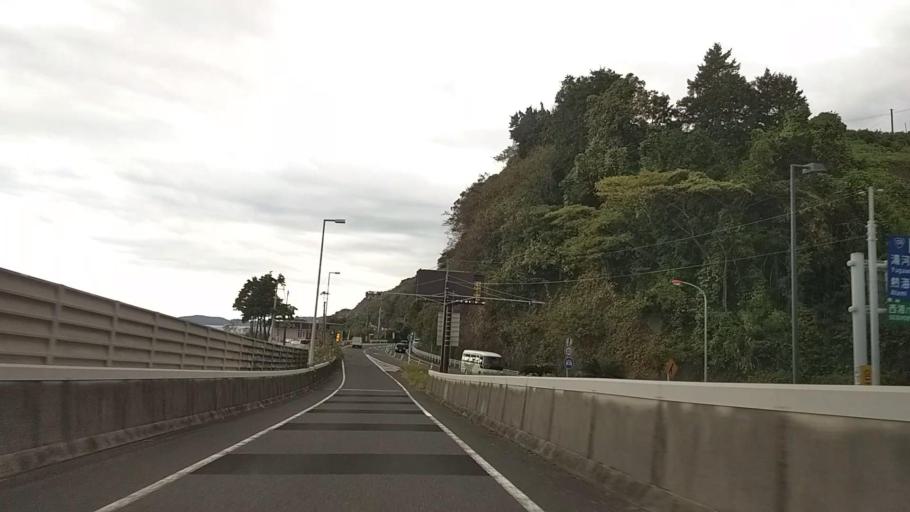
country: JP
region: Kanagawa
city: Odawara
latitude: 35.2287
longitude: 139.1426
